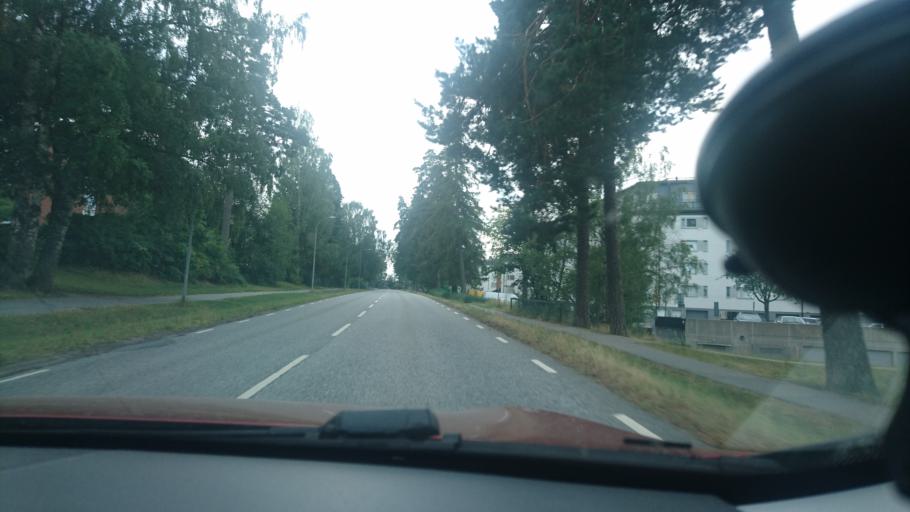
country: SE
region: Stockholm
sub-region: Upplands Vasby Kommun
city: Upplands Vaesby
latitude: 59.5275
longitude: 17.9202
